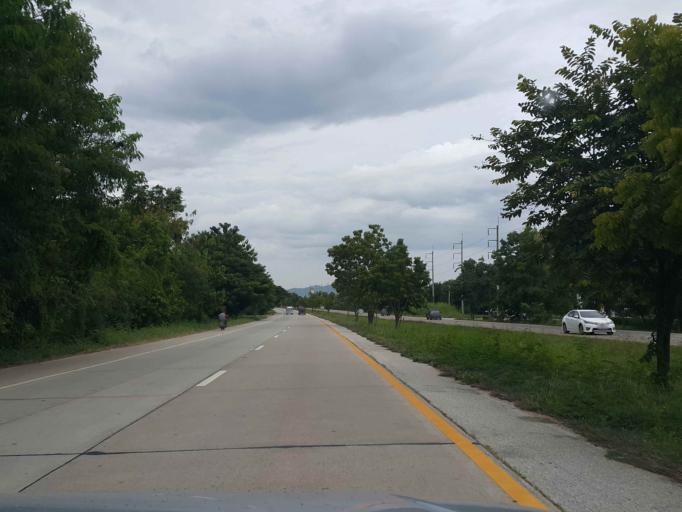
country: TH
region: Lampang
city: Lampang
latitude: 18.2935
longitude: 99.4214
